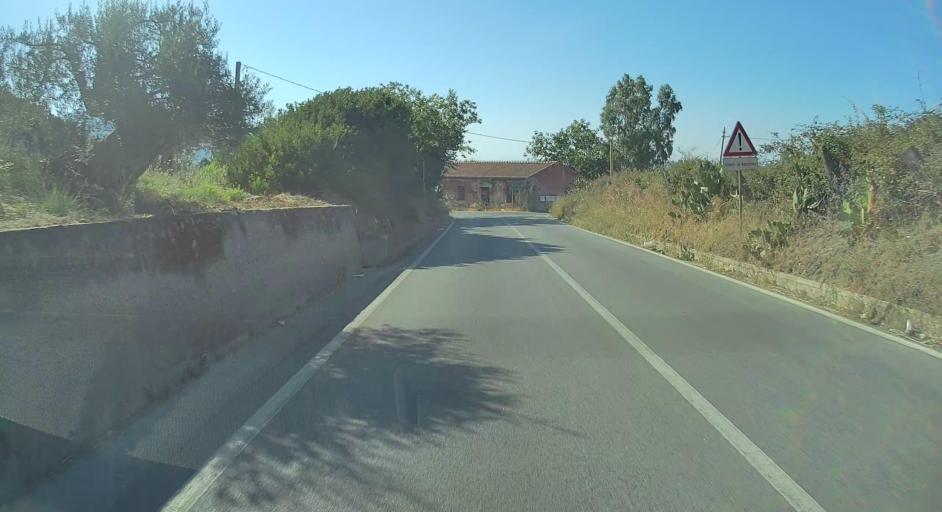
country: IT
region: Sicily
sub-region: Messina
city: Oliveri
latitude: 38.1414
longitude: 15.0163
